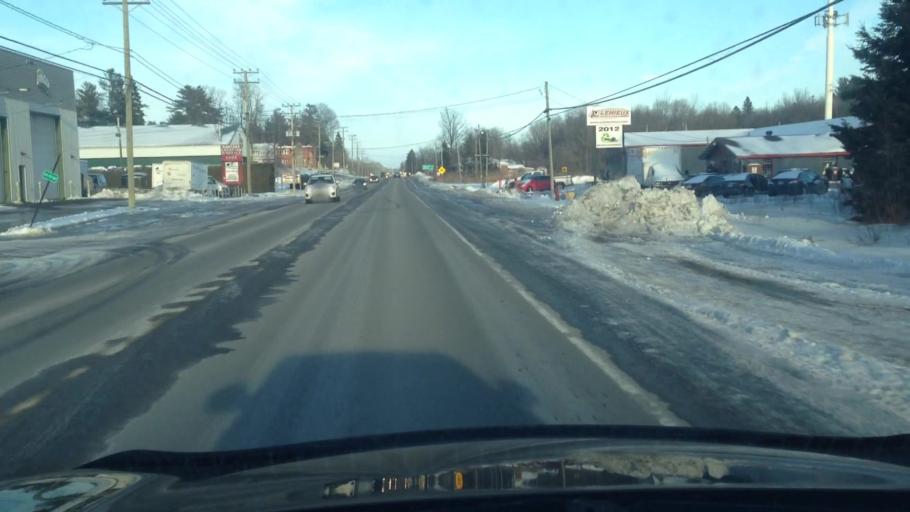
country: CA
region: Quebec
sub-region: Laurentides
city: Saint-Jerome
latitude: 45.7774
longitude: -73.9636
